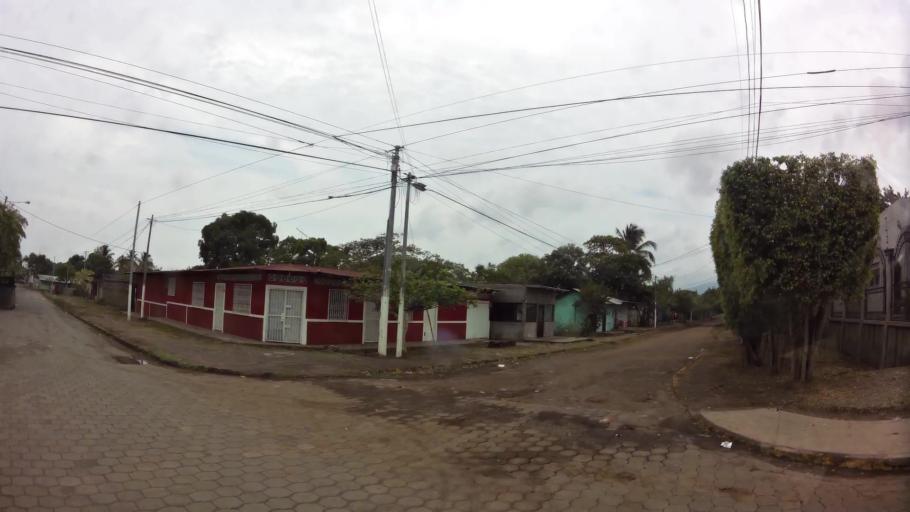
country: NI
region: Granada
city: Granada
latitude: 11.9416
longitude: -85.9564
